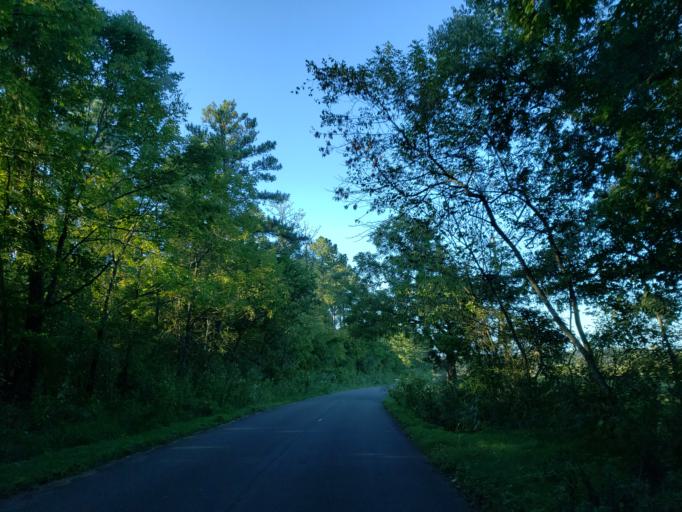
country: US
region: Georgia
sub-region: Bartow County
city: Rydal
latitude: 34.3192
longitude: -84.7300
